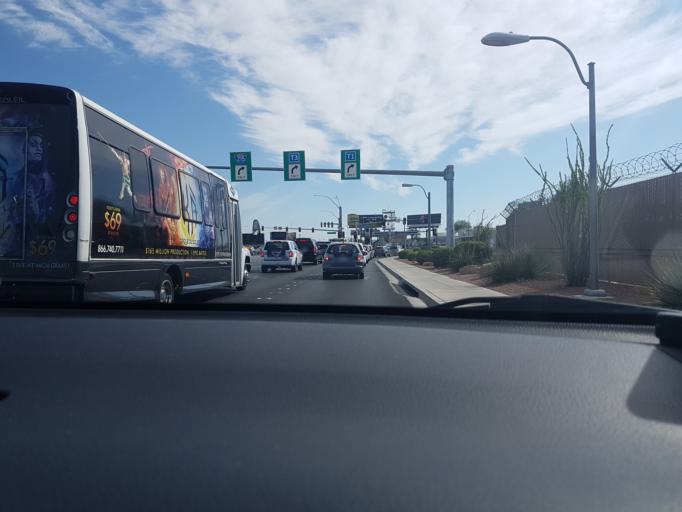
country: US
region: Nevada
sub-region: Clark County
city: Paradise
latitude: 36.1008
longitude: -115.1511
